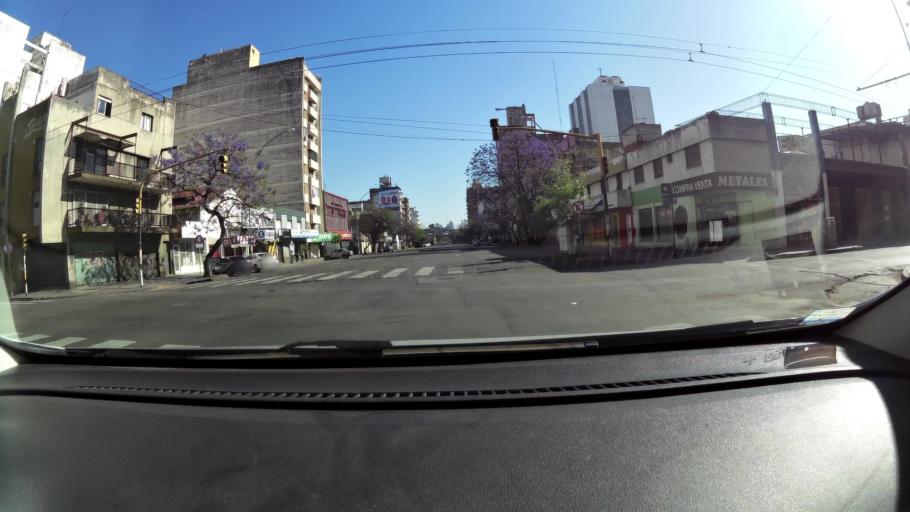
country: AR
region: Cordoba
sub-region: Departamento de Capital
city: Cordoba
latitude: -31.4137
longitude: -64.1785
